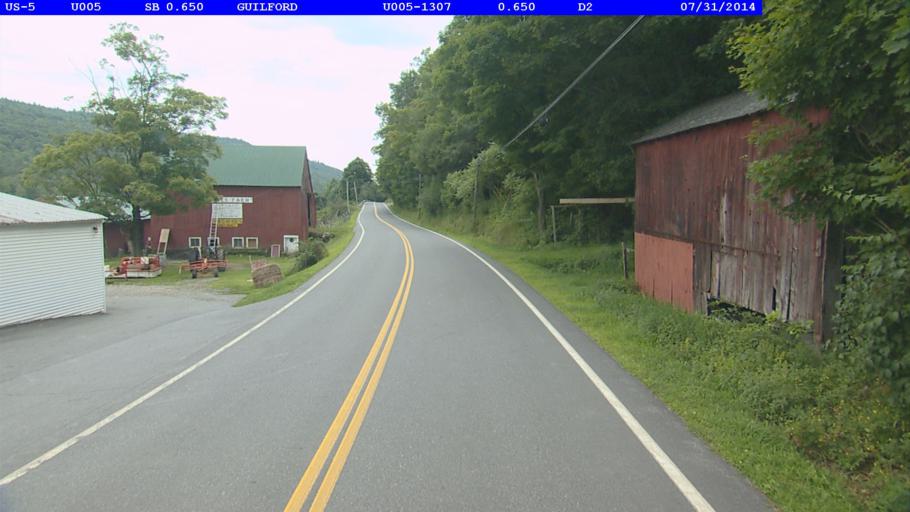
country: US
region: Massachusetts
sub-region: Franklin County
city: Bernardston
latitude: 42.7394
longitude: -72.5728
